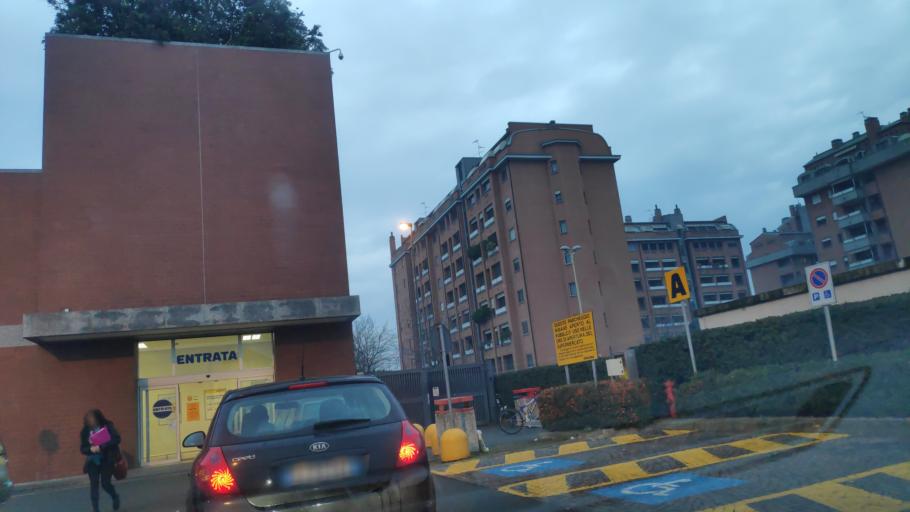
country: IT
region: Lombardy
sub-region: Citta metropolitana di Milano
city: Romano Banco
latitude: 45.4332
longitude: 9.1208
